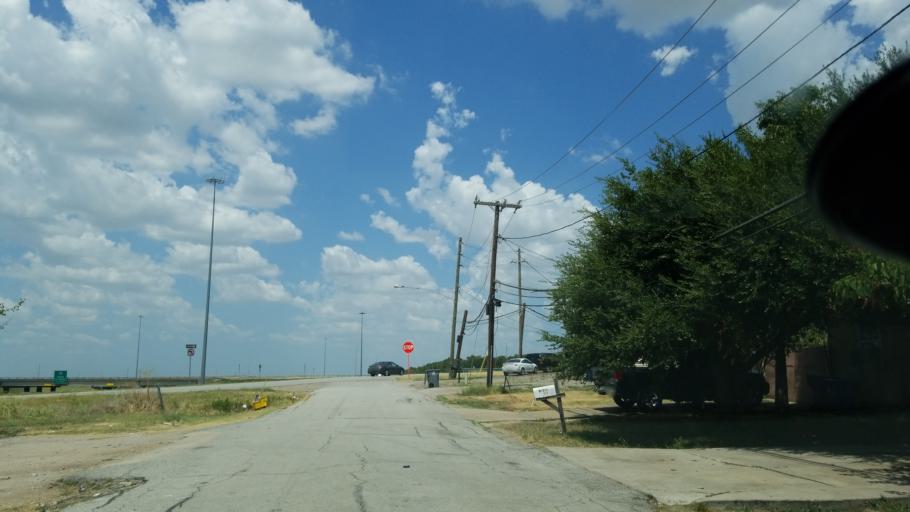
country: US
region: Texas
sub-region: Dallas County
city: Cockrell Hill
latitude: 32.7456
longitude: -96.9177
